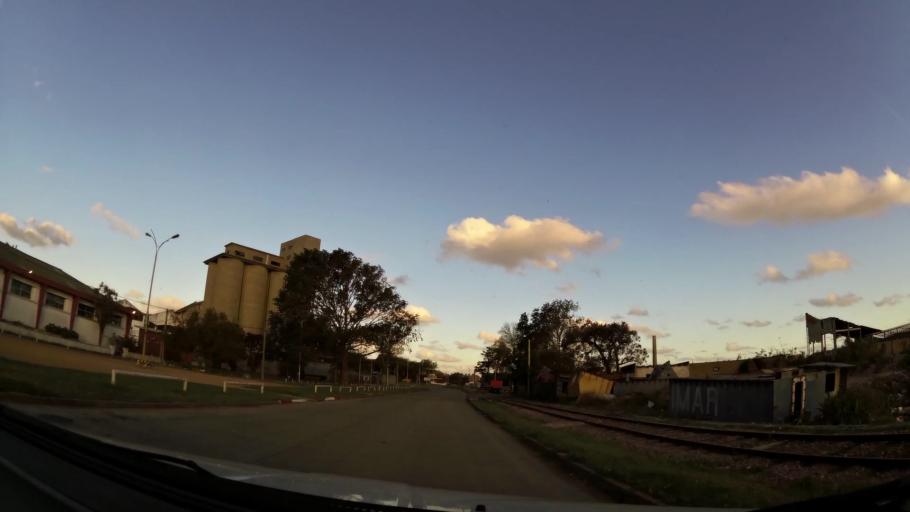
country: UY
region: Montevideo
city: Montevideo
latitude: -34.8729
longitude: -56.2209
